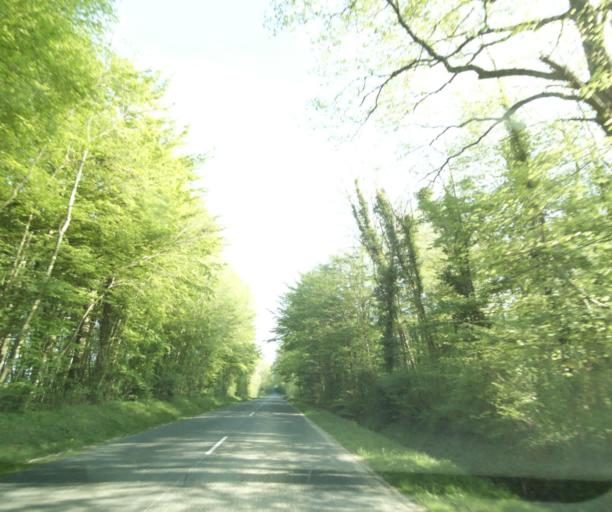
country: FR
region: Ile-de-France
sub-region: Departement de Seine-et-Marne
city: Vernou-la-Celle-sur-Seine
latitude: 48.4436
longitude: 2.8575
